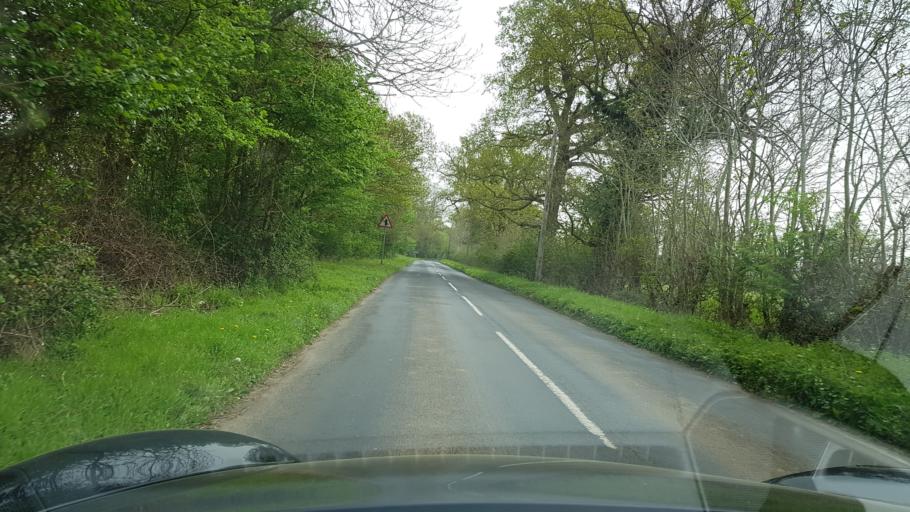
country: GB
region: England
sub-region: Surrey
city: Ripley
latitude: 51.2929
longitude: -0.4795
